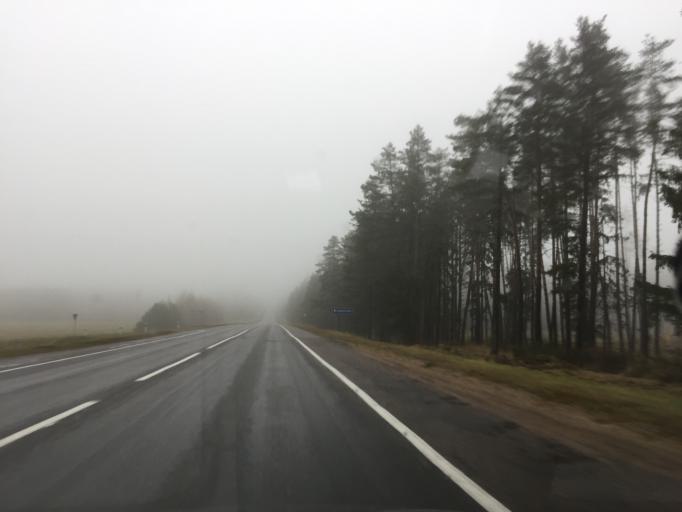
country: BY
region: Mogilev
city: Kamyennyya Lavy
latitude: 54.1328
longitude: 30.4574
